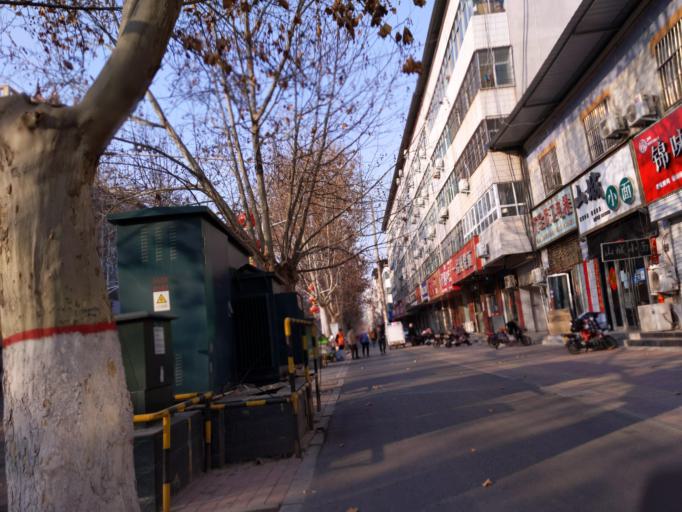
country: CN
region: Henan Sheng
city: Puyang
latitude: 35.7656
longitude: 115.0324
